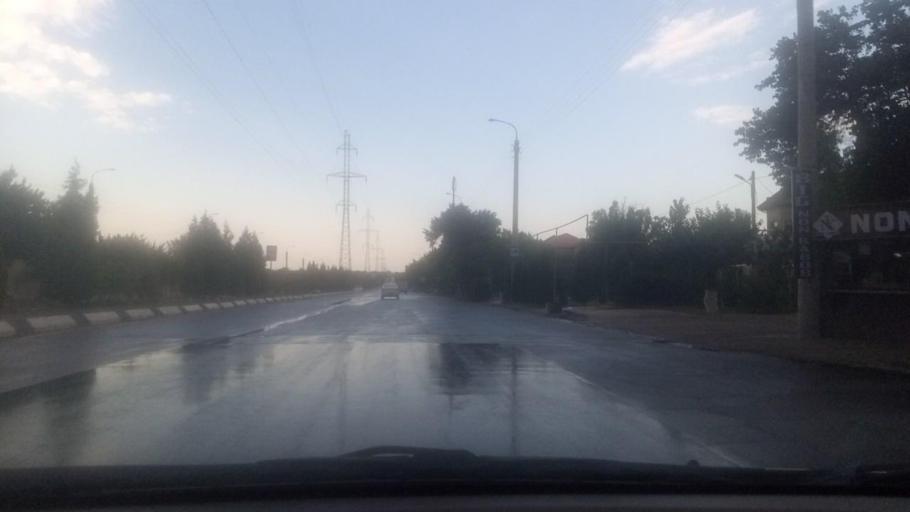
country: UZ
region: Toshkent Shahri
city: Tashkent
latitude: 41.3165
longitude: 69.1932
